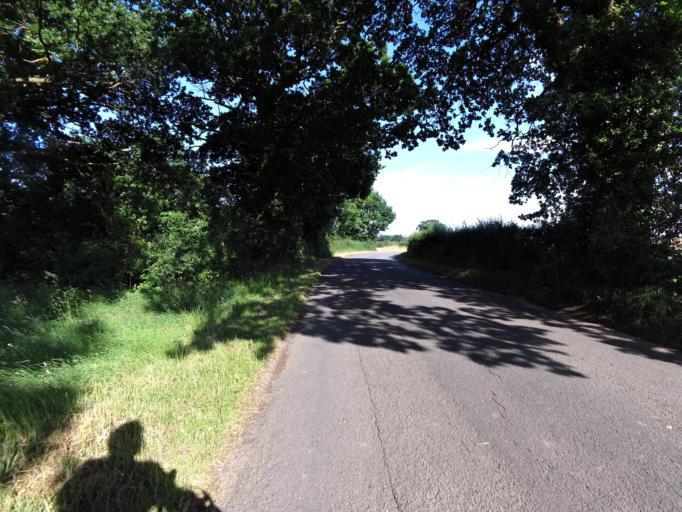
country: GB
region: England
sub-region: Suffolk
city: Leiston
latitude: 52.2736
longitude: 1.5640
